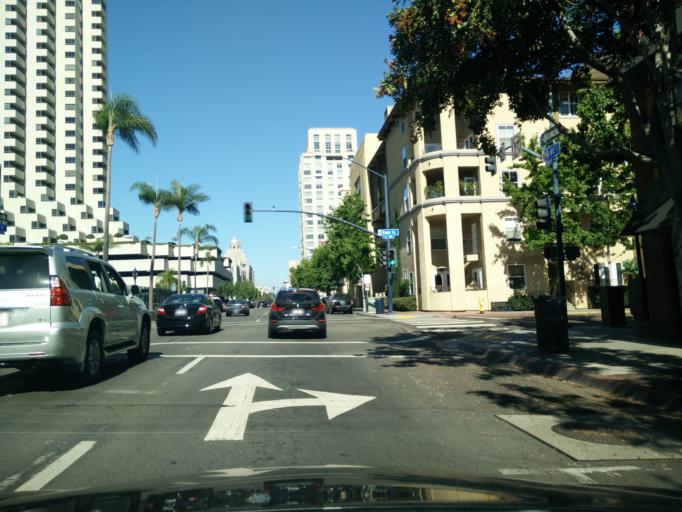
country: US
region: California
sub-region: San Diego County
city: San Diego
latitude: 32.7125
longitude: -117.1668
